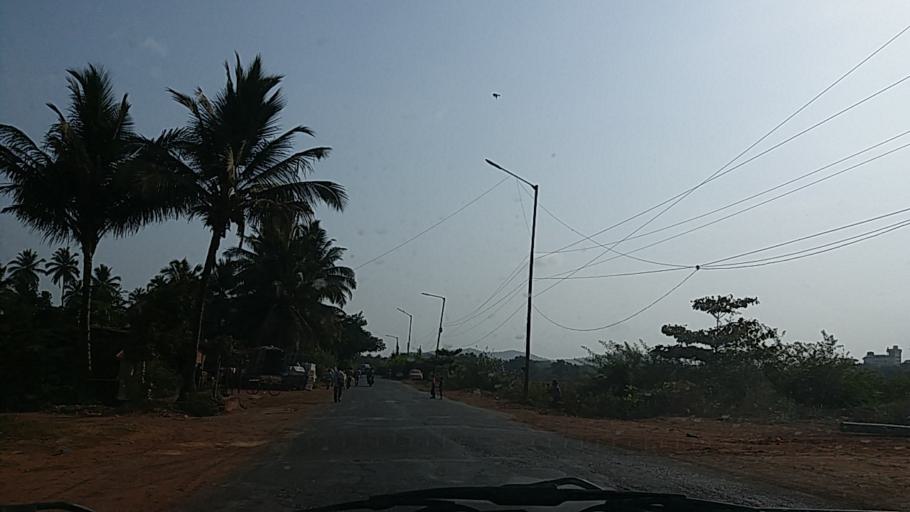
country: IN
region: Goa
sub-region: South Goa
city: Madgaon
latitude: 15.2613
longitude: 73.9692
